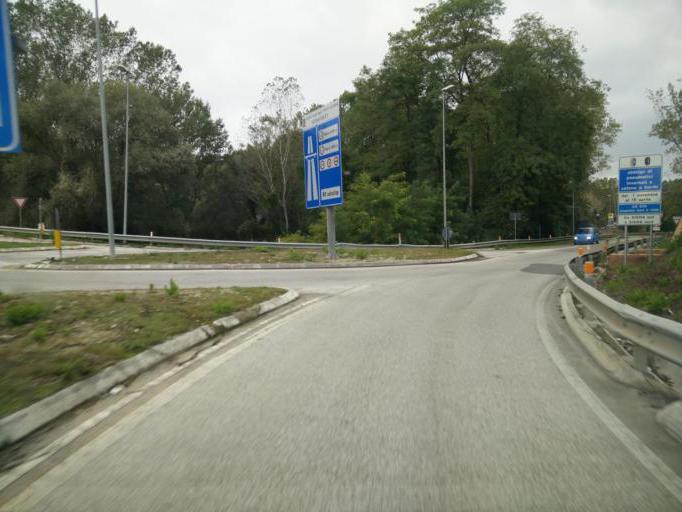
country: IT
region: Tuscany
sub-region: Provincia di Siena
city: Siena
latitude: 43.3091
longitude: 11.3151
